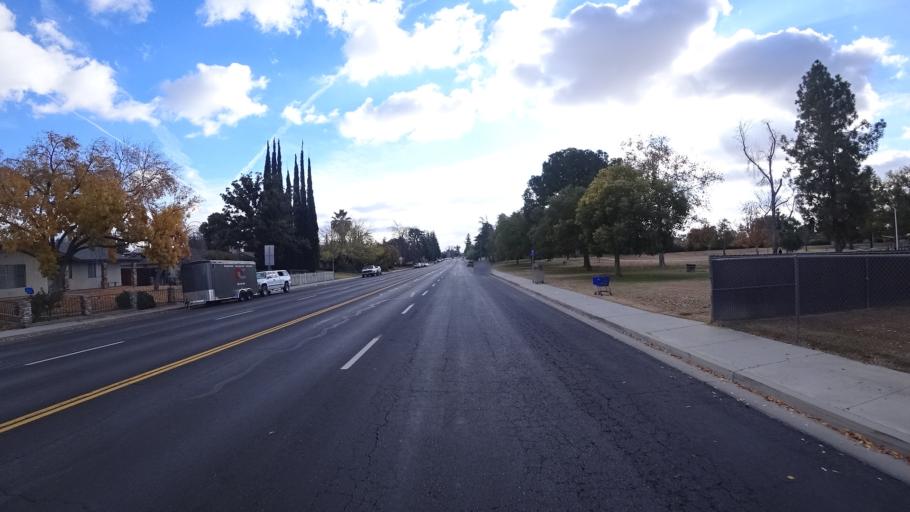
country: US
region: California
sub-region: Kern County
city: Bakersfield
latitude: 35.3285
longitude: -119.0658
